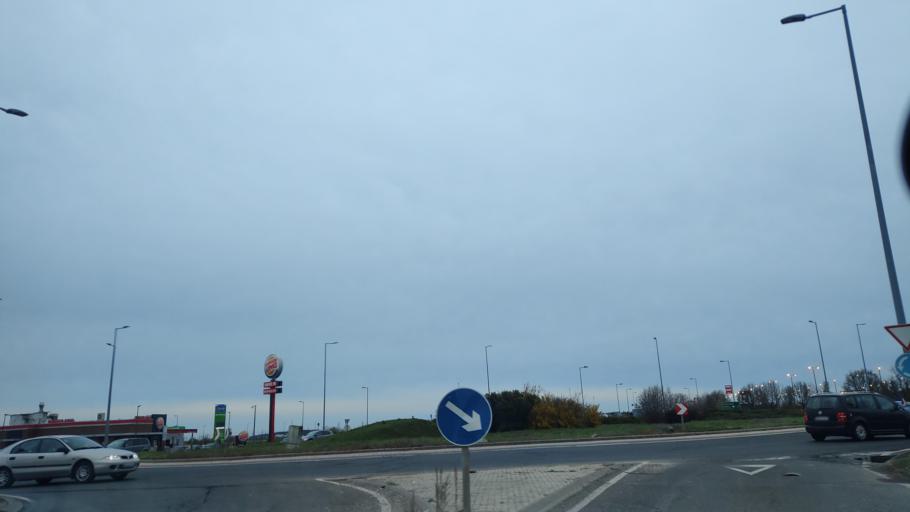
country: HU
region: Vas
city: Szombathely
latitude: 47.2427
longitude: 16.6528
